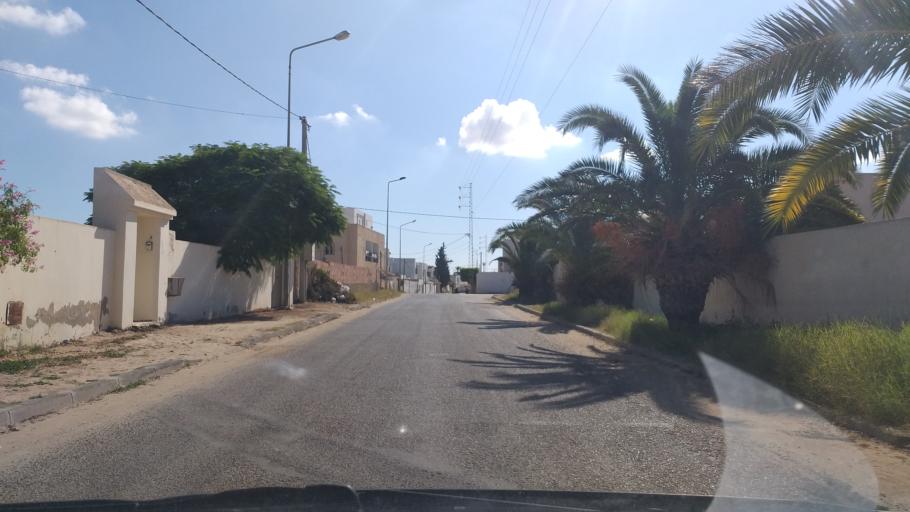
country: TN
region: Safaqis
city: Al Qarmadah
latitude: 34.8020
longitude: 10.7720
